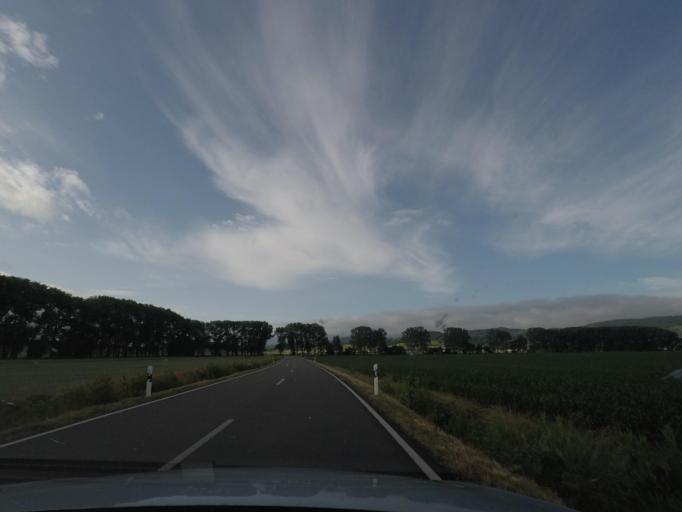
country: DE
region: Saxony-Anhalt
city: Derenburg
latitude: 51.8433
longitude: 10.9140
